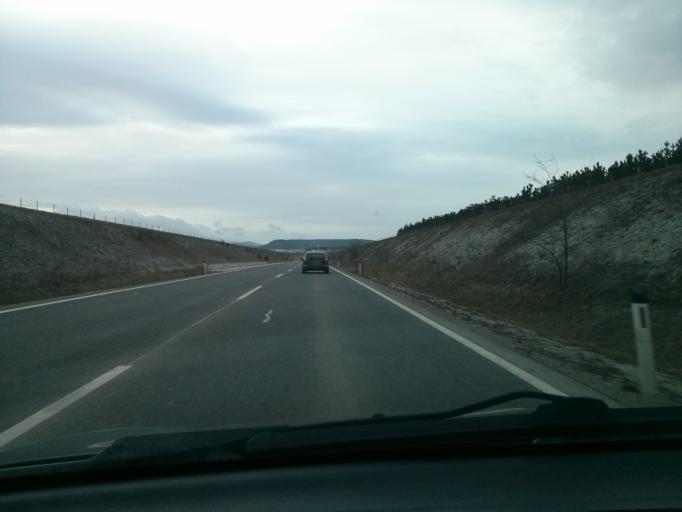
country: AT
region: Lower Austria
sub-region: Politischer Bezirk Wiener Neustadt
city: Theresienfeld
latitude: 47.8496
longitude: 16.2237
